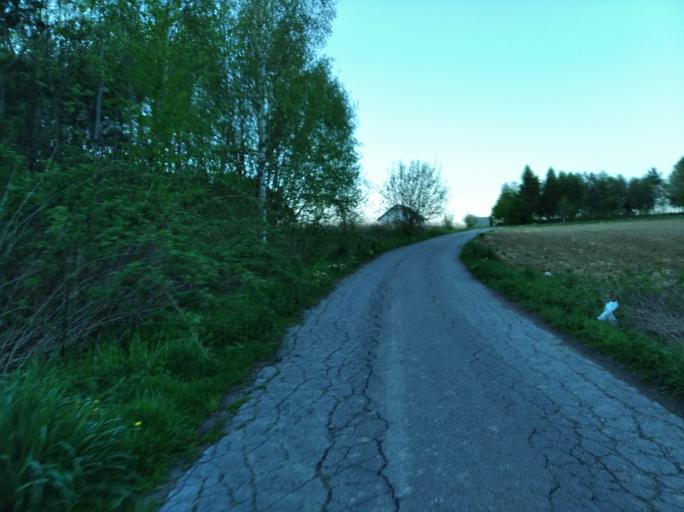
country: PL
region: Subcarpathian Voivodeship
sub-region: Powiat strzyzowski
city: Strzyzow
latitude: 49.8544
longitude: 21.7664
